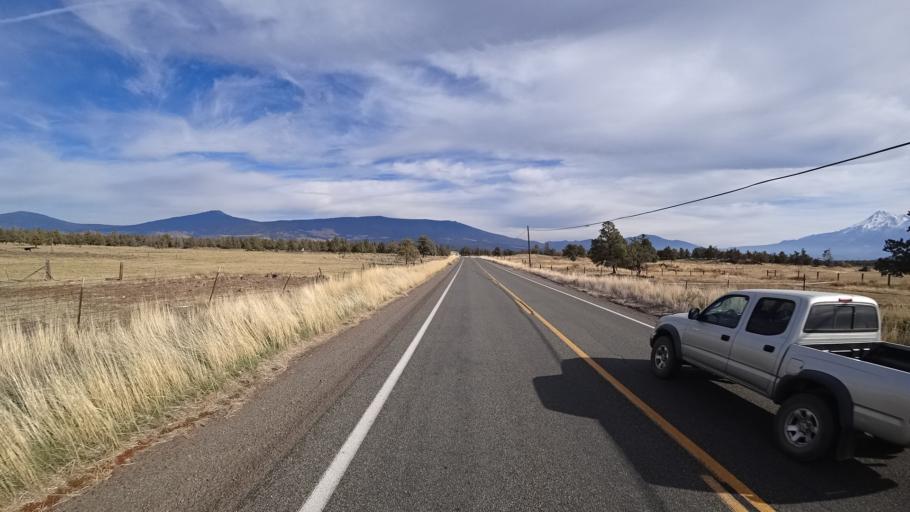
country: US
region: California
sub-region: Siskiyou County
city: Montague
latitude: 41.6239
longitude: -122.3877
